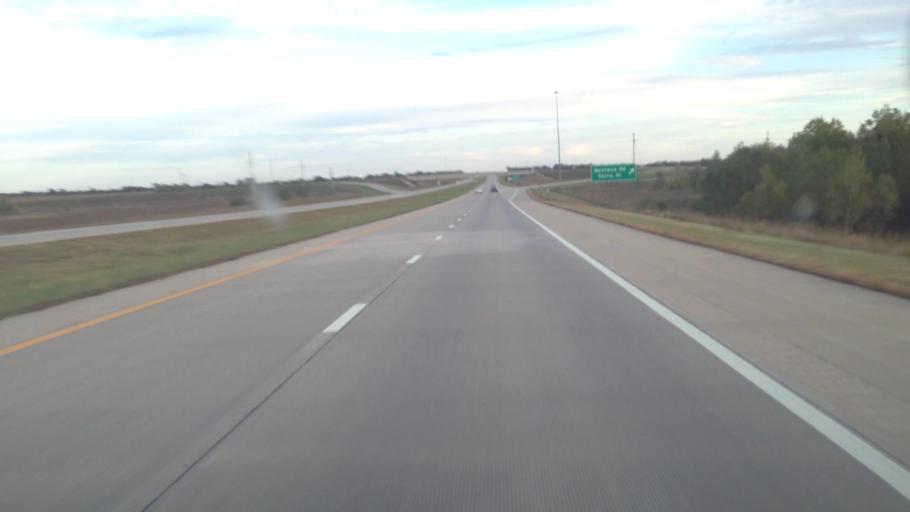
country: US
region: Kansas
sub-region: Franklin County
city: Ottawa
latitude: 38.6695
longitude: -95.2556
